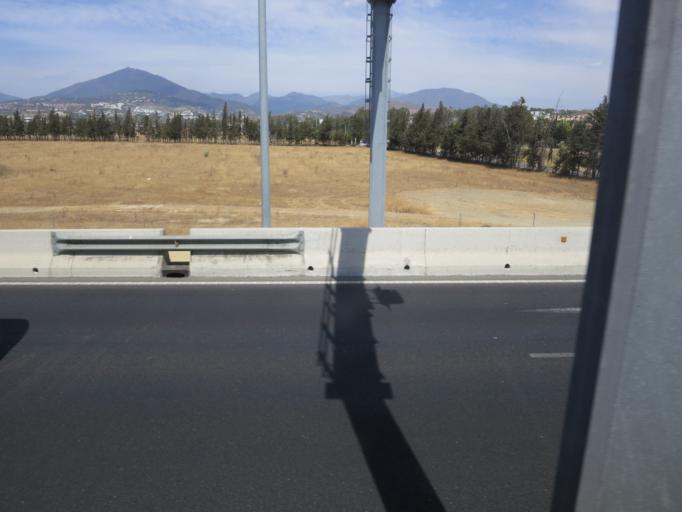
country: ES
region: Andalusia
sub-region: Provincia de Malaga
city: Benahavis
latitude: 36.4862
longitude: -4.9758
